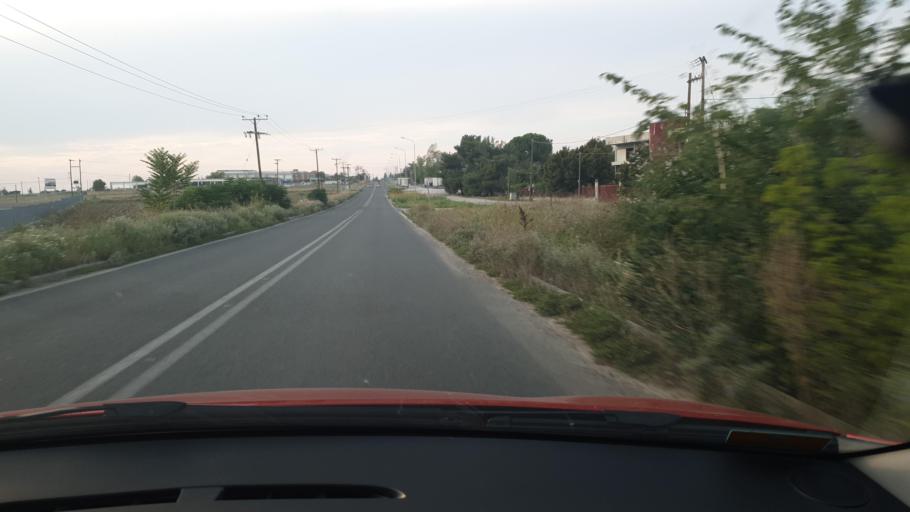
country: GR
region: Central Macedonia
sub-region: Nomos Thessalonikis
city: Thermi
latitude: 40.5272
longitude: 23.0466
